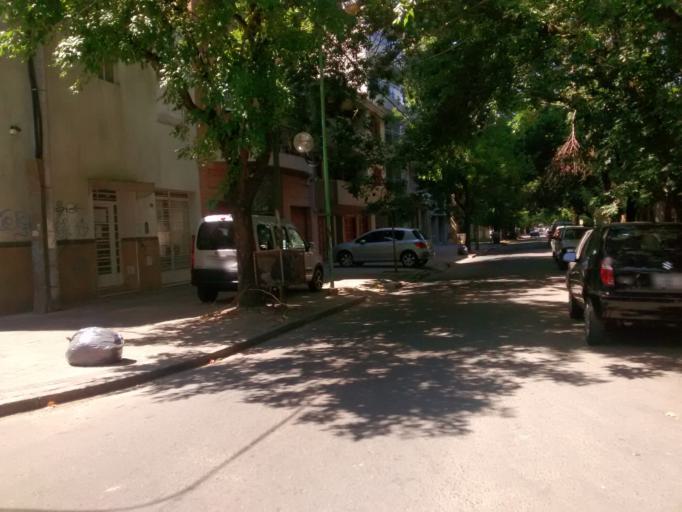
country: AR
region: Buenos Aires
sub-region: Partido de La Plata
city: La Plata
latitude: -34.9256
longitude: -57.9445
